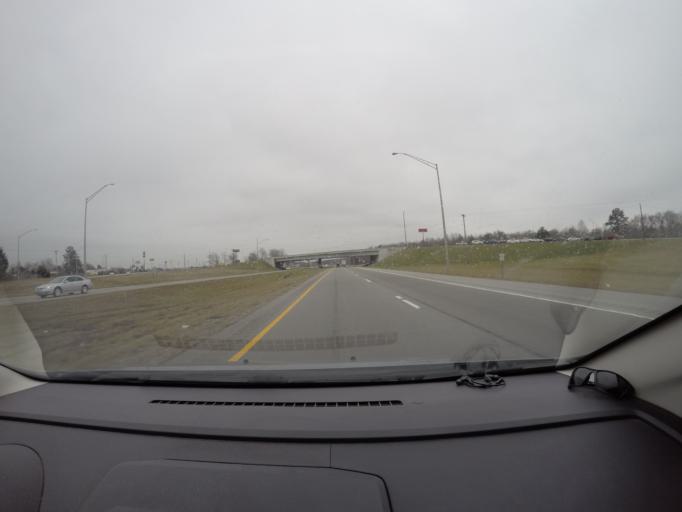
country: US
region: Tennessee
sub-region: Coffee County
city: Manchester
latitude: 35.4591
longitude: -86.0527
